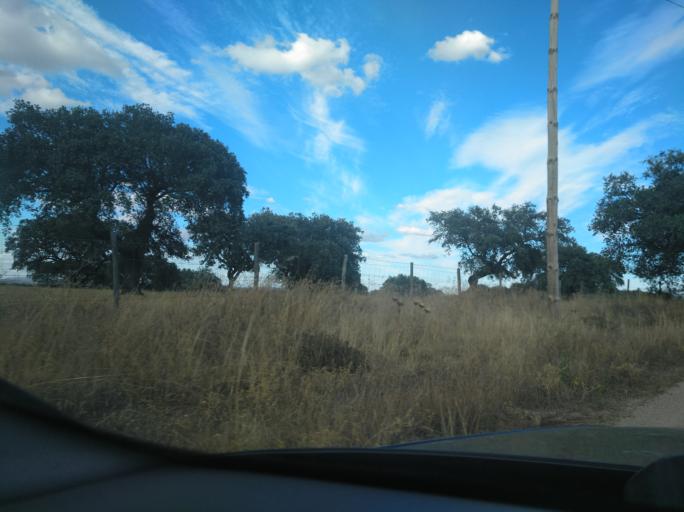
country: PT
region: Portalegre
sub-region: Campo Maior
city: Campo Maior
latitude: 39.0701
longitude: -7.1097
